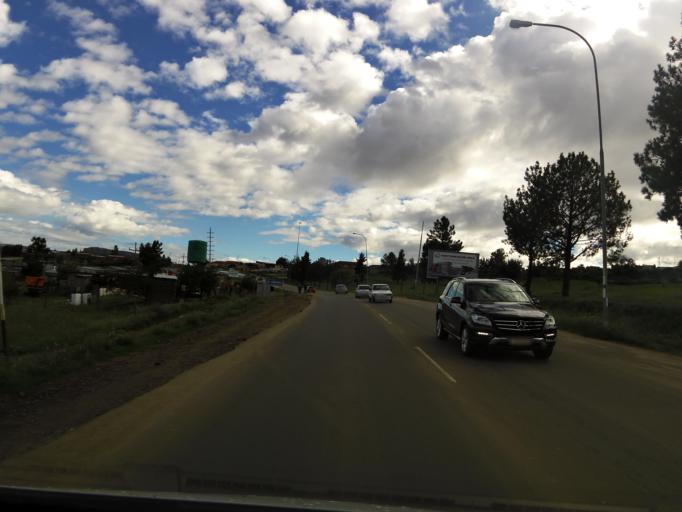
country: LS
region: Maseru
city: Maseru
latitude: -29.2990
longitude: 27.5176
